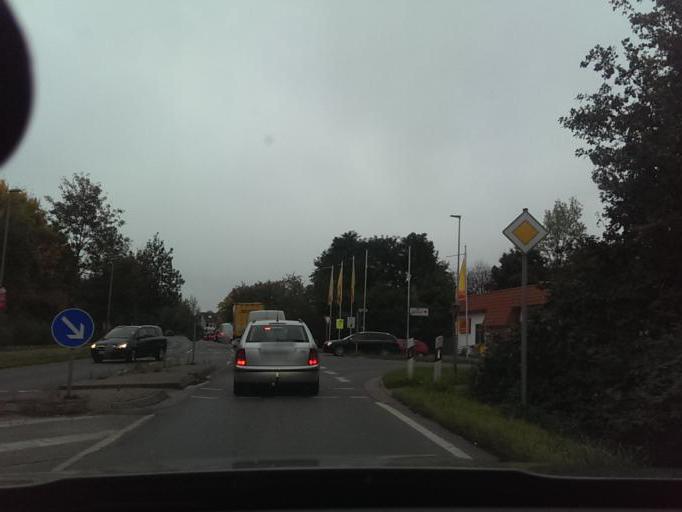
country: DE
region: Lower Saxony
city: Seelze
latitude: 52.3993
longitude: 9.5909
